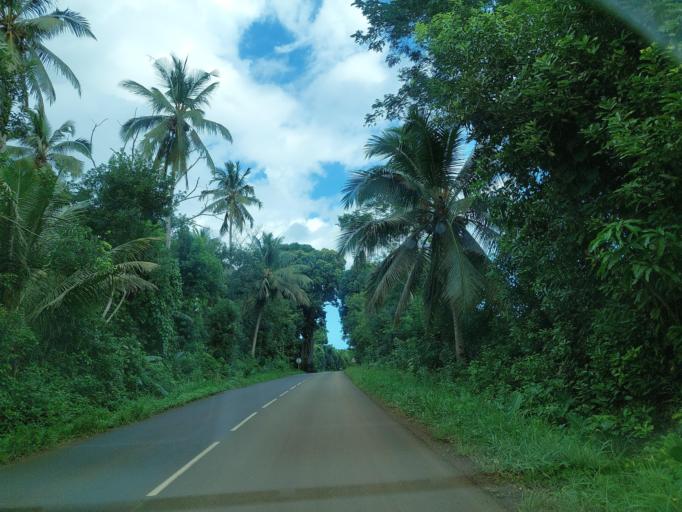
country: YT
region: M'Tsangamouji
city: M'Tsangamouji
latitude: -12.7519
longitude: 45.1146
